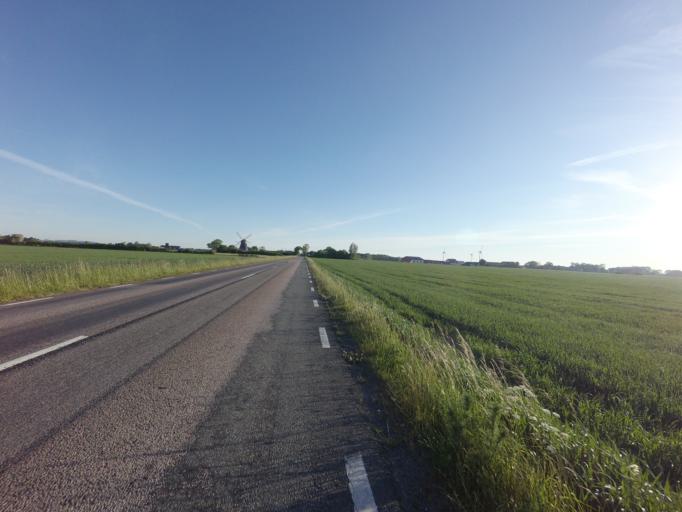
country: SE
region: Skane
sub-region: Helsingborg
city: Odakra
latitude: 56.1889
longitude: 12.6757
